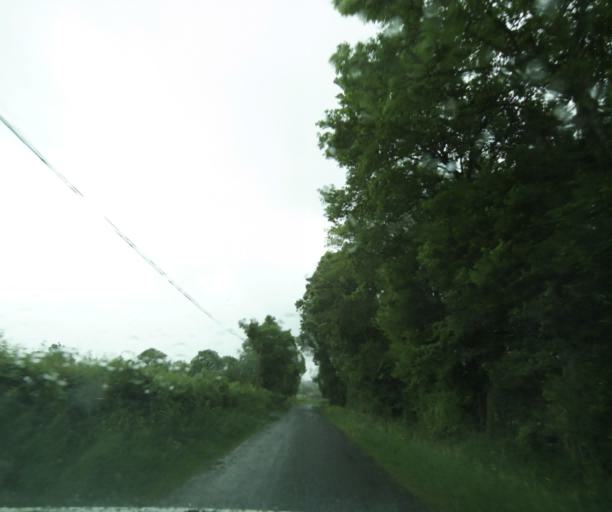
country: FR
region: Bourgogne
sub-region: Departement de Saone-et-Loire
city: Palinges
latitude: 46.5292
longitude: 4.2724
